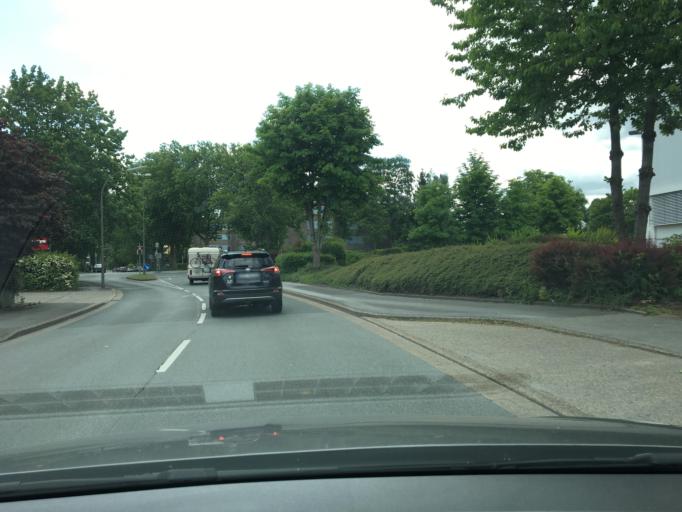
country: DE
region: North Rhine-Westphalia
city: Witten
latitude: 51.5056
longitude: 7.3657
